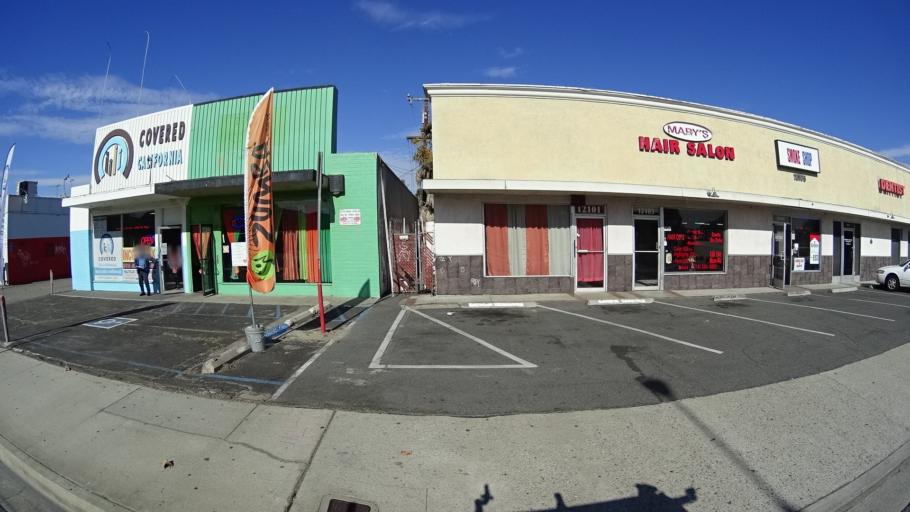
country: US
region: California
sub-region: Orange County
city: Garden Grove
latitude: 33.7743
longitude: -117.9220
